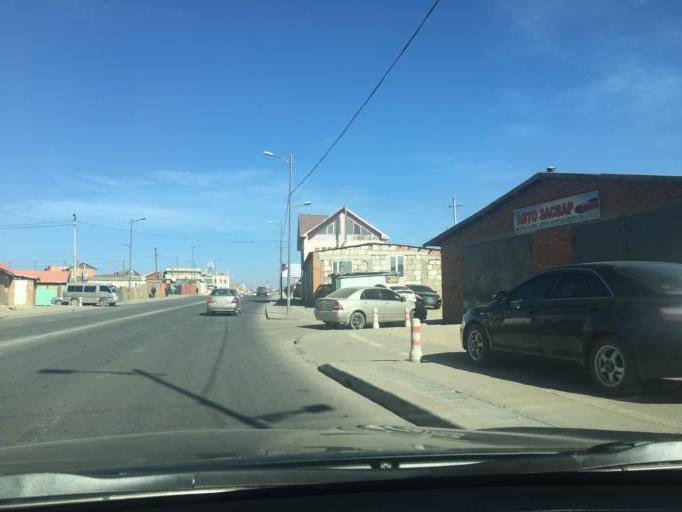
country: MN
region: Ulaanbaatar
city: Ulaanbaatar
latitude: 47.9162
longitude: 106.7805
